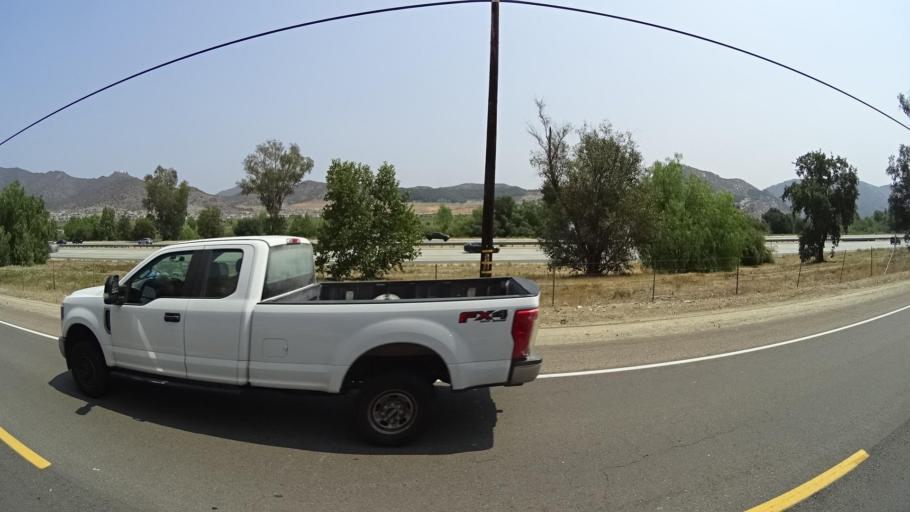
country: US
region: California
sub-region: San Diego County
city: Rainbow
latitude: 33.3512
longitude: -117.1597
